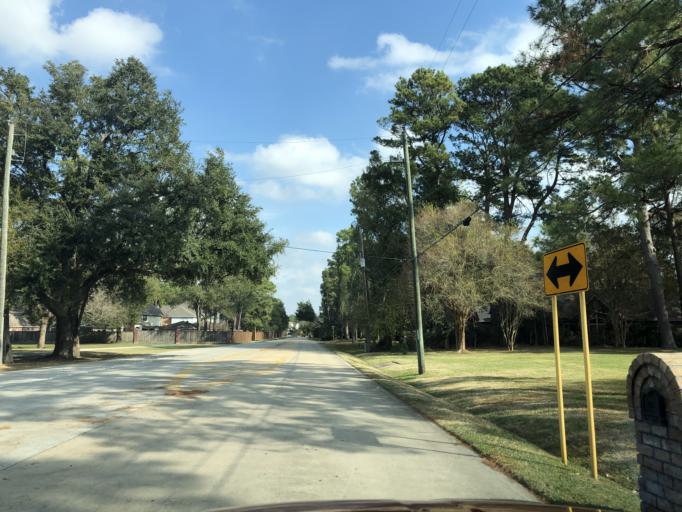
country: US
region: Texas
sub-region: Harris County
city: Tomball
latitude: 30.0277
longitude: -95.5475
